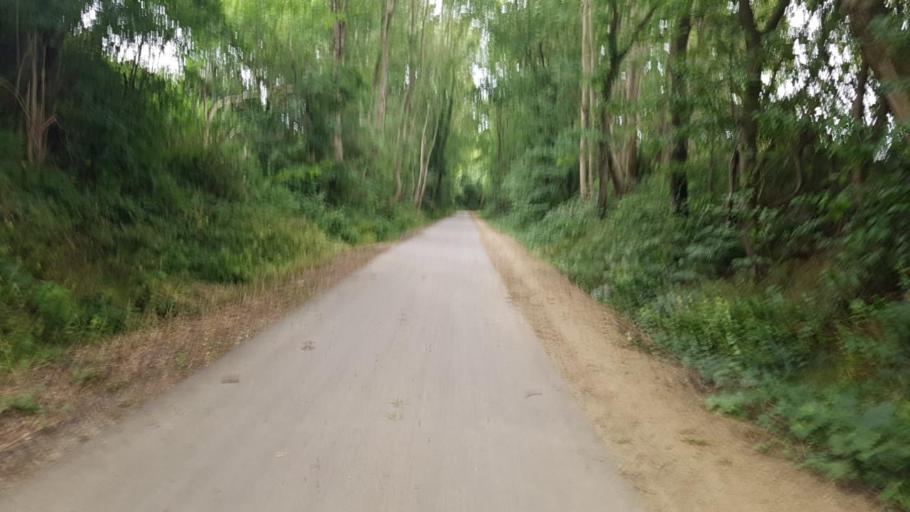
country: BE
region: Wallonia
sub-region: Province de Liege
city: Plombieres
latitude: 50.7348
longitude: 5.9522
